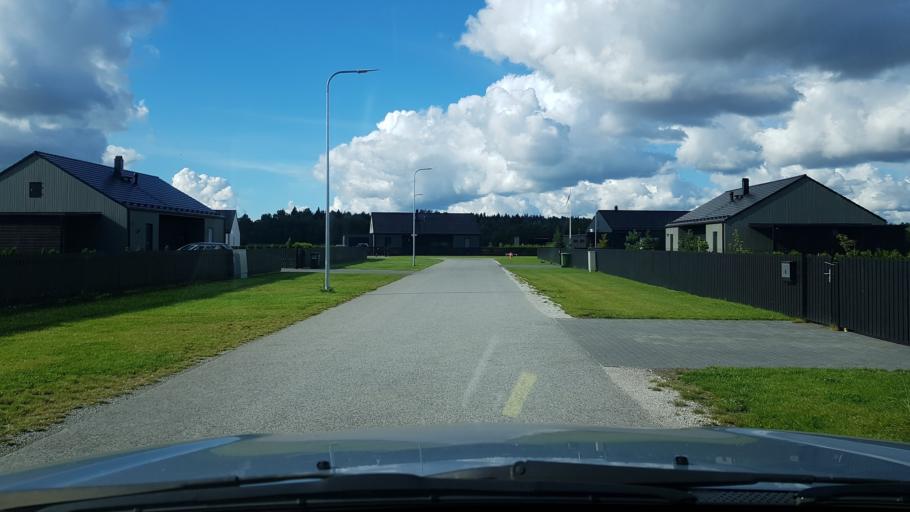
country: EE
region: Harju
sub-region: Kiili vald
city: Kiili
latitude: 59.3620
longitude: 24.8051
